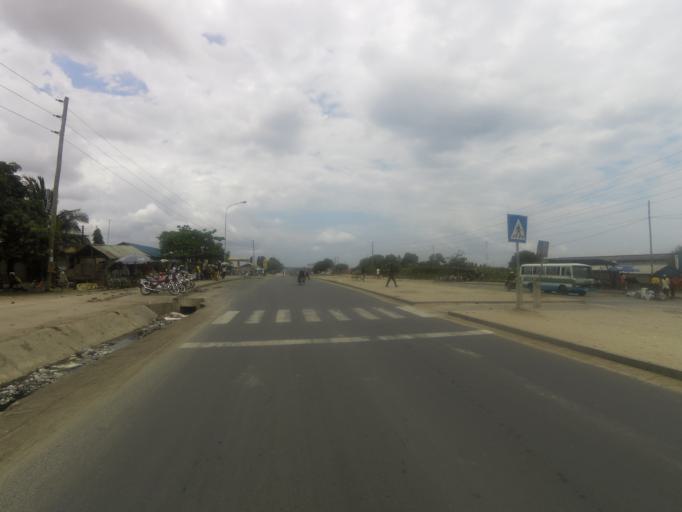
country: TZ
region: Pwani
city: Vikindu
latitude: -6.9287
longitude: 39.2719
